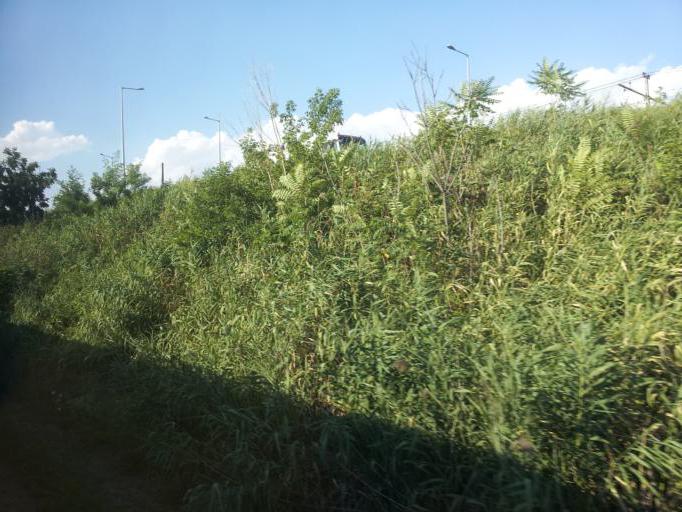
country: HU
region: Budapest
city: Budapest XX. keruelet
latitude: 47.4280
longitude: 19.1024
